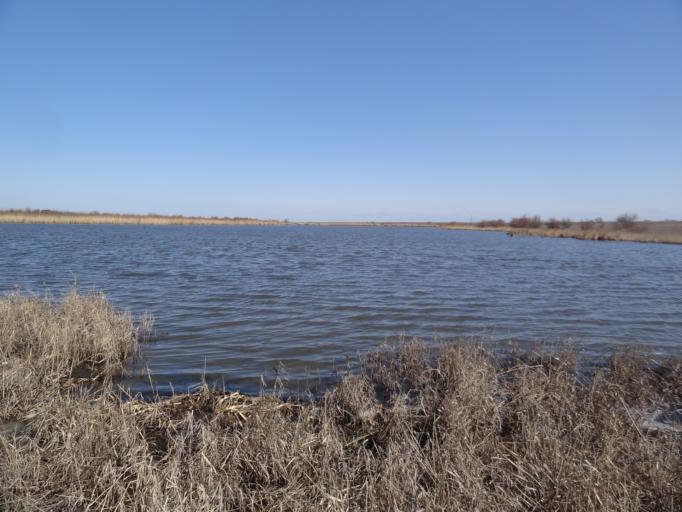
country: RU
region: Saratov
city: Shumeyka
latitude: 51.4199
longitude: 46.3098
